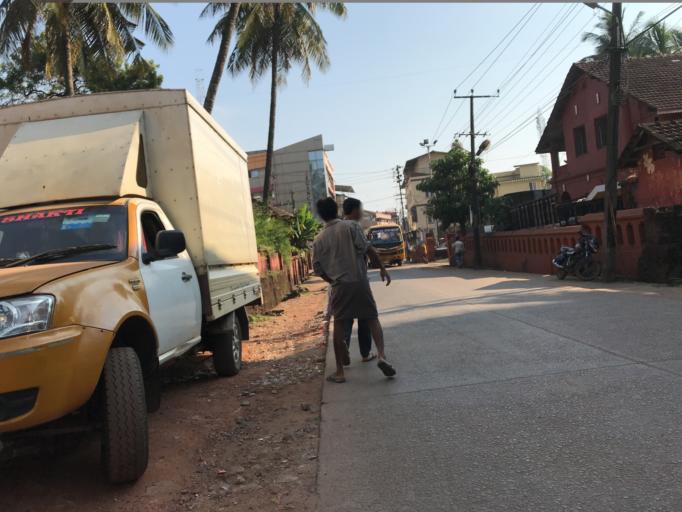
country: IN
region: Karnataka
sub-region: Dakshina Kannada
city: Mangalore
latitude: 12.8646
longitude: 74.8338
